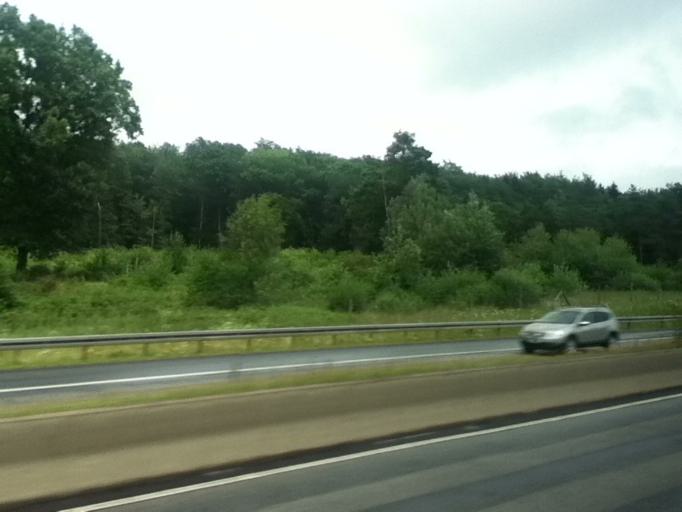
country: DE
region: Hesse
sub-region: Regierungsbezirk Giessen
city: Grunberg
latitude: 50.6390
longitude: 8.9477
